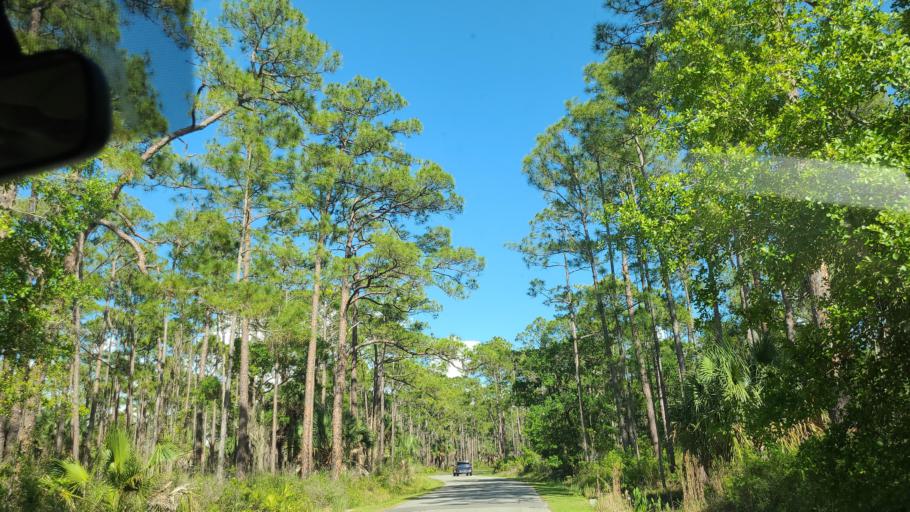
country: US
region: Florida
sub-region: Polk County
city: Babson Park
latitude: 27.9532
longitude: -81.3638
